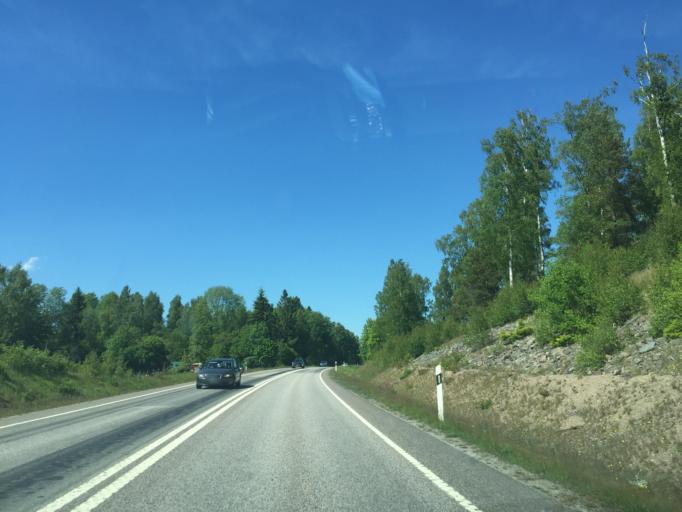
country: SE
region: OEstergoetland
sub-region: Motala Kommun
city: Motala
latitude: 58.6341
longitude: 14.9611
